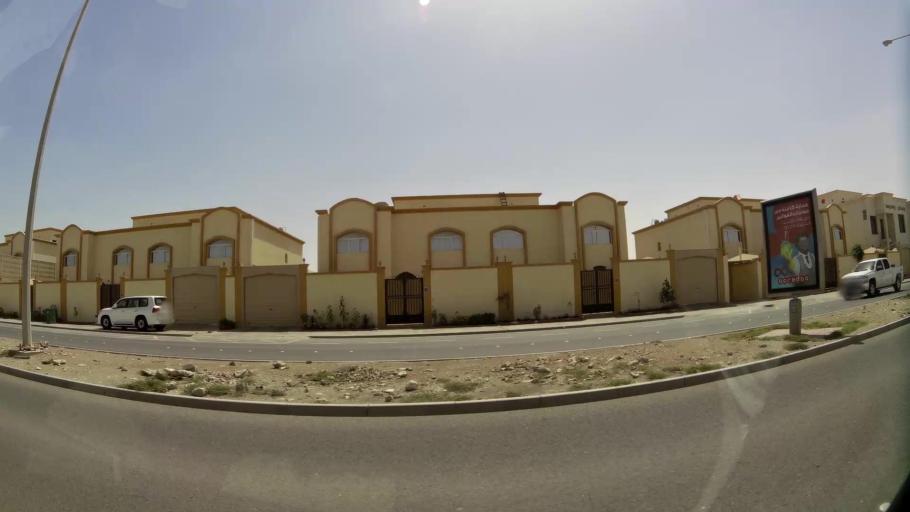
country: QA
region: Baladiyat Umm Salal
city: Umm Salal Muhammad
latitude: 25.3652
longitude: 51.4325
